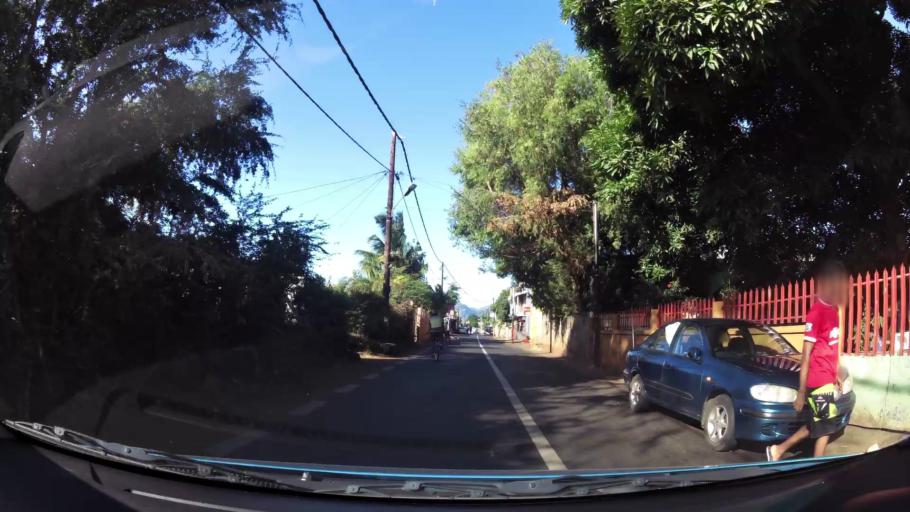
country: MU
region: Black River
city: Petite Riviere
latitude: -20.1967
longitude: 57.4435
